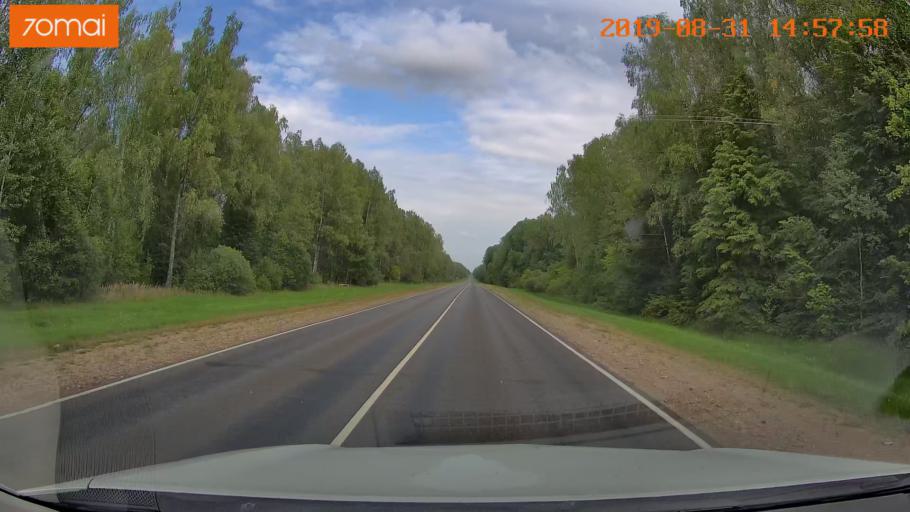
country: RU
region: Kaluga
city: Spas-Demensk
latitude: 54.3142
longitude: 33.9700
